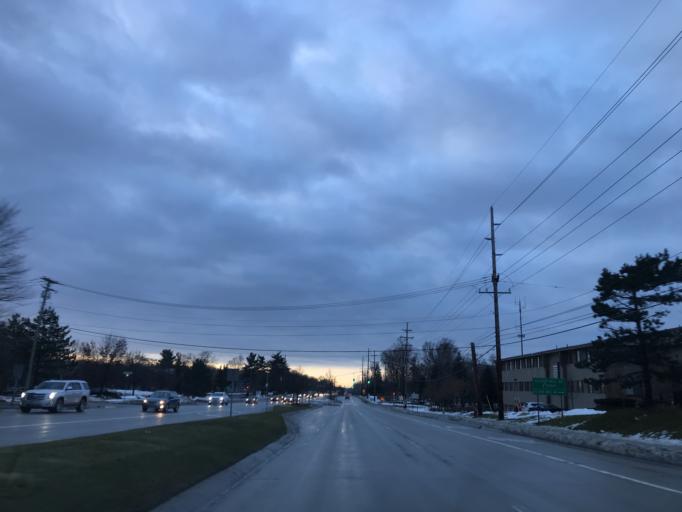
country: US
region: Michigan
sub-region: Oakland County
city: Farmington Hills
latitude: 42.4863
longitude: -83.3581
